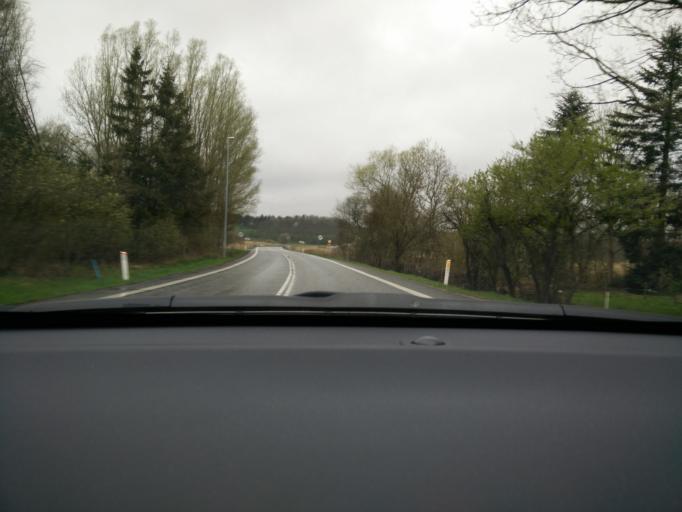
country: DK
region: Central Jutland
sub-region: Viborg Kommune
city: Viborg
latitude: 56.5129
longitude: 9.3079
